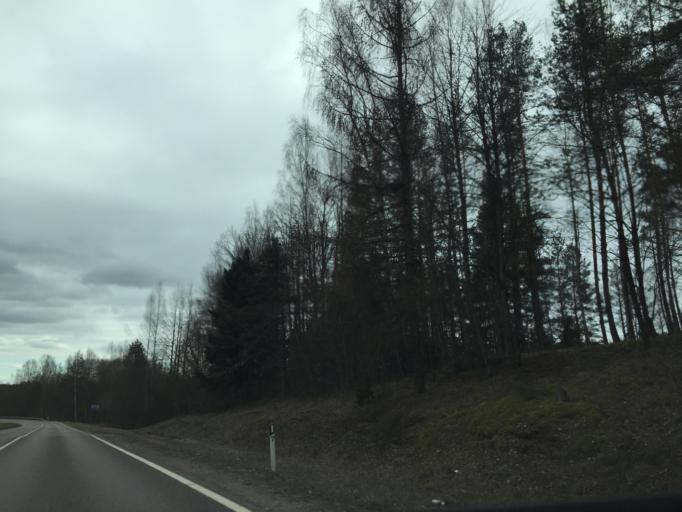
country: LV
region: Kraslavas Rajons
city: Kraslava
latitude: 55.8962
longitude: 27.1269
